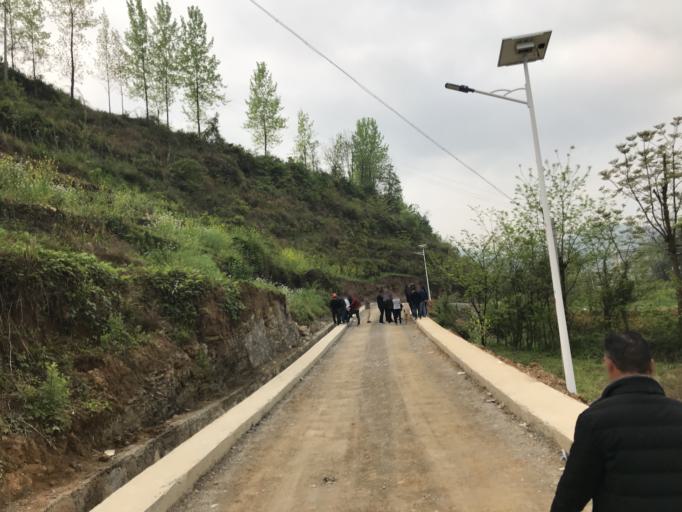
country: CN
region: Guizhou Sheng
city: Longquan
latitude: 28.2039
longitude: 108.0540
